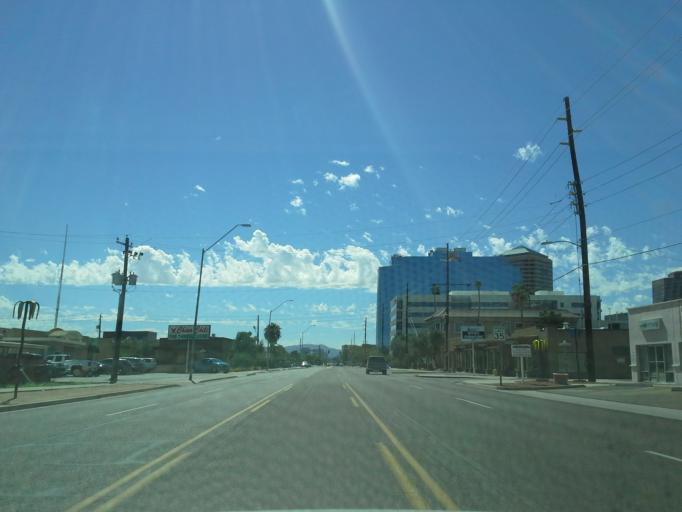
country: US
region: Arizona
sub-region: Maricopa County
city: Phoenix
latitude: 33.4865
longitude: -112.0695
